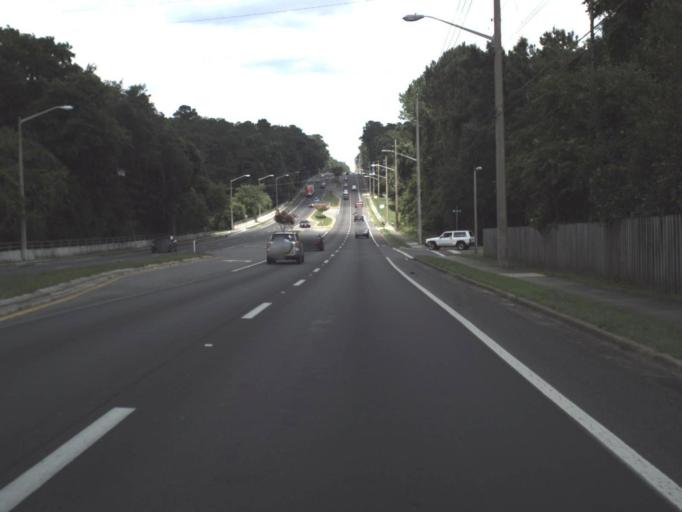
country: US
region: Florida
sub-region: Alachua County
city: Alachua
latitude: 29.6887
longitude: -82.4241
